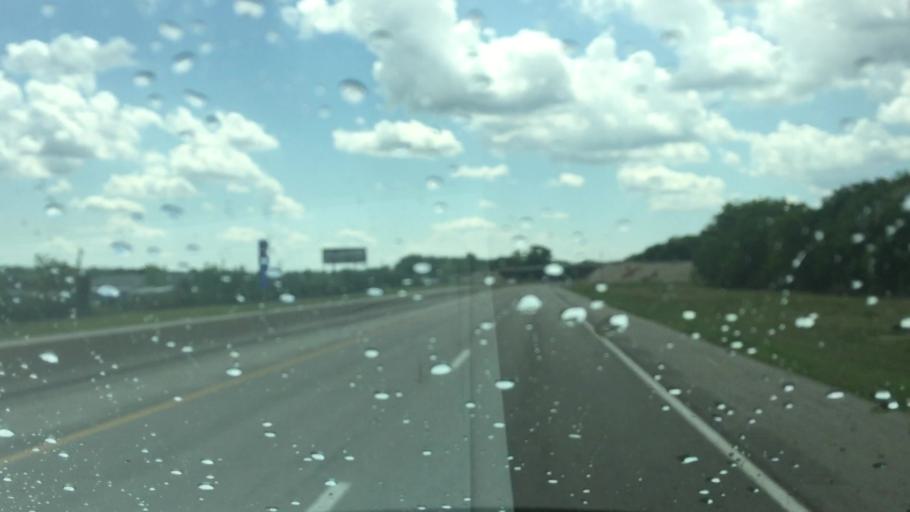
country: US
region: Kansas
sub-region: Shawnee County
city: Topeka
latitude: 38.9704
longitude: -95.7137
